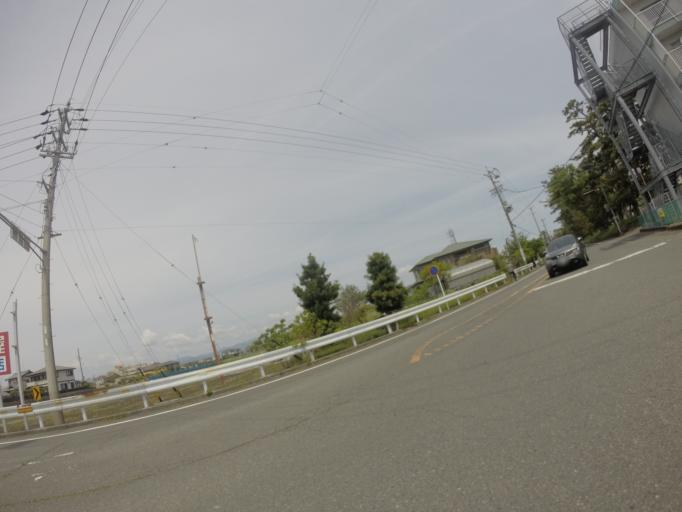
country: JP
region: Shizuoka
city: Yaizu
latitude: 34.8331
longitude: 138.3335
